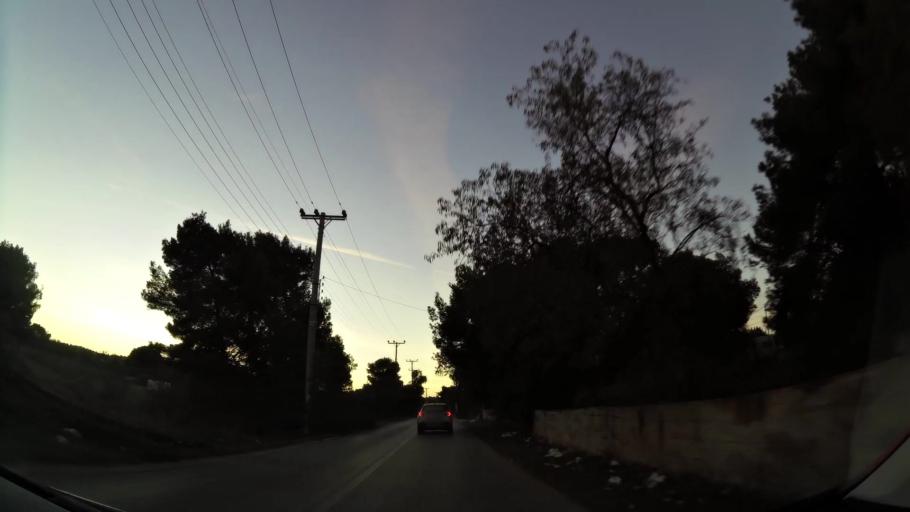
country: GR
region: Attica
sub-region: Nomarchia Anatolikis Attikis
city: Rafina
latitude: 37.9994
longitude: 23.9949
